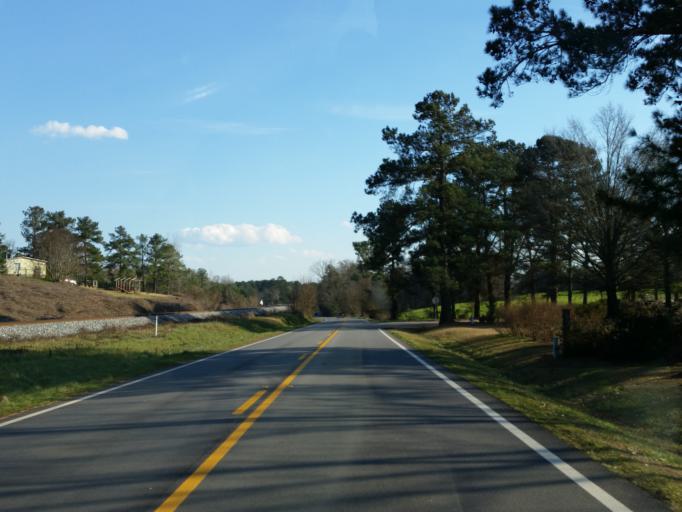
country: US
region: Georgia
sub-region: Monroe County
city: Forsyth
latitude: 32.9751
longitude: -83.8719
